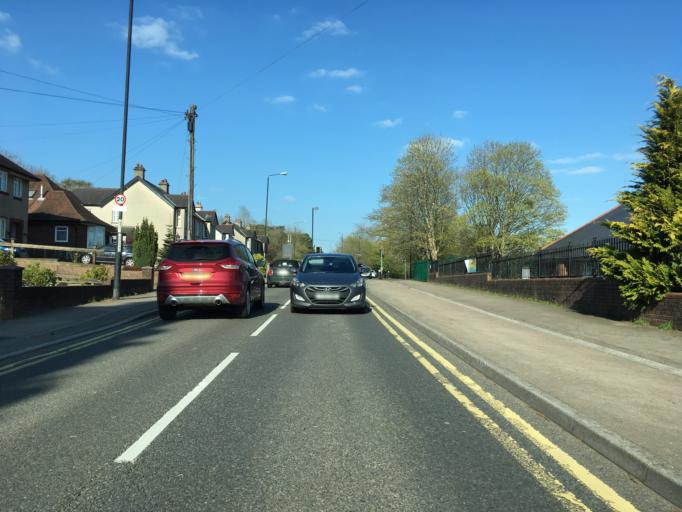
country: GB
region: Wales
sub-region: Monmouthshire
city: Usk
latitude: 51.7051
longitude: -2.8996
